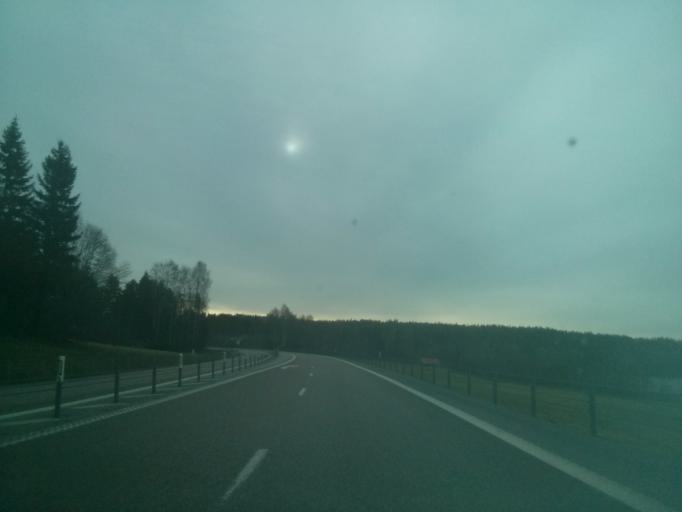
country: SE
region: Vaesternorrland
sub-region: Timra Kommun
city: Soraker
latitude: 62.5576
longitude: 17.6649
